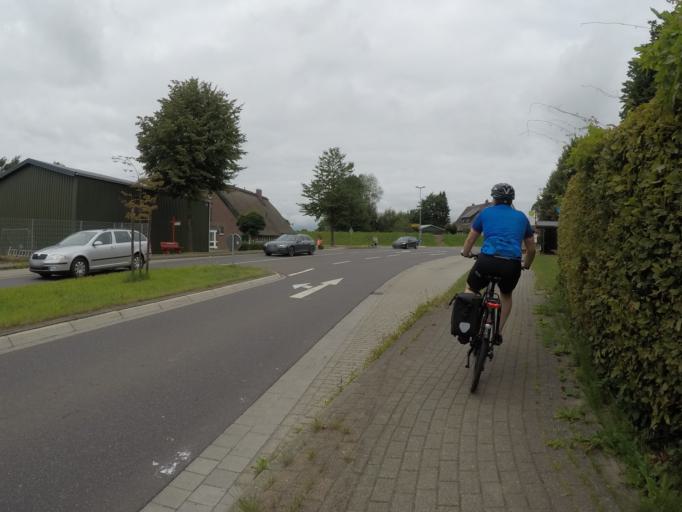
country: DE
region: Lower Saxony
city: Mittelnkirchen
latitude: 53.5397
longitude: 9.6242
